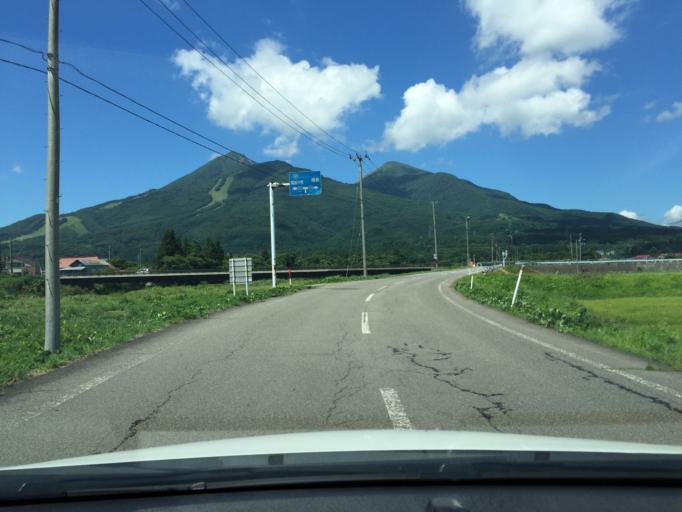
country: JP
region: Fukushima
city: Inawashiro
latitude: 37.5686
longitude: 140.1255
